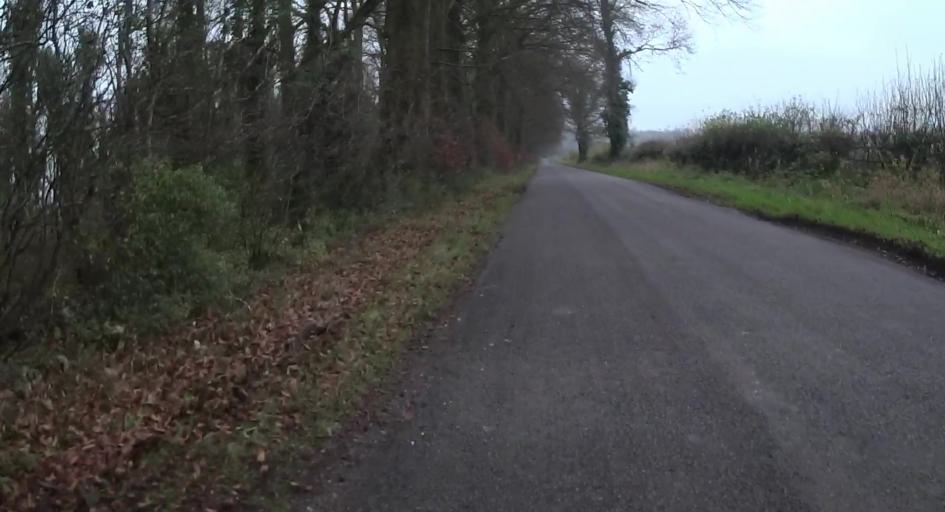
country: GB
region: England
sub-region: Hampshire
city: Kings Worthy
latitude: 51.1226
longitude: -1.2113
